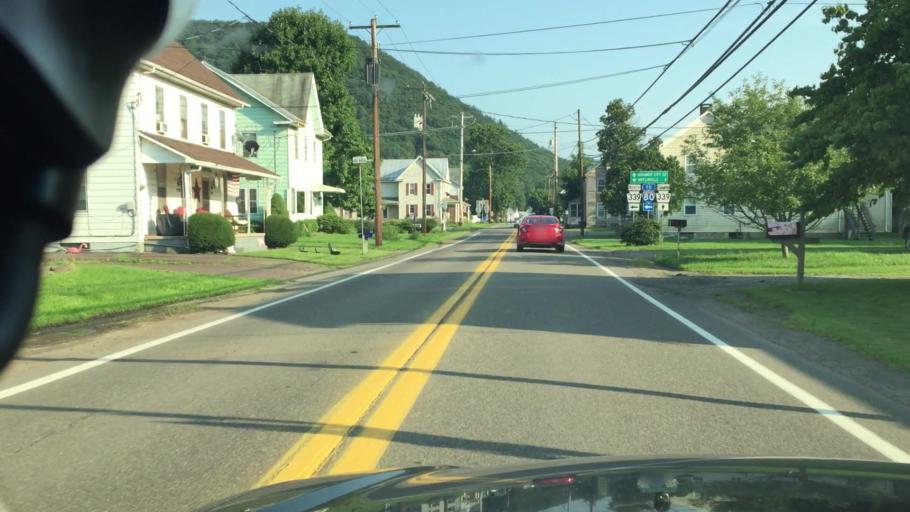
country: US
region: Pennsylvania
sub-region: Columbia County
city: Almedia
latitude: 40.9766
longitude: -76.3746
